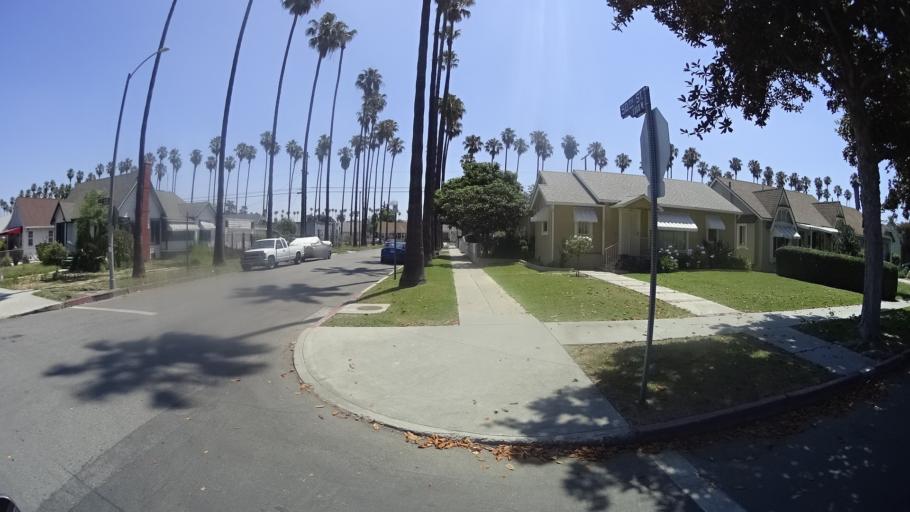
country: US
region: California
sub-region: Los Angeles County
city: View Park-Windsor Hills
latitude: 33.9977
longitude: -118.3247
